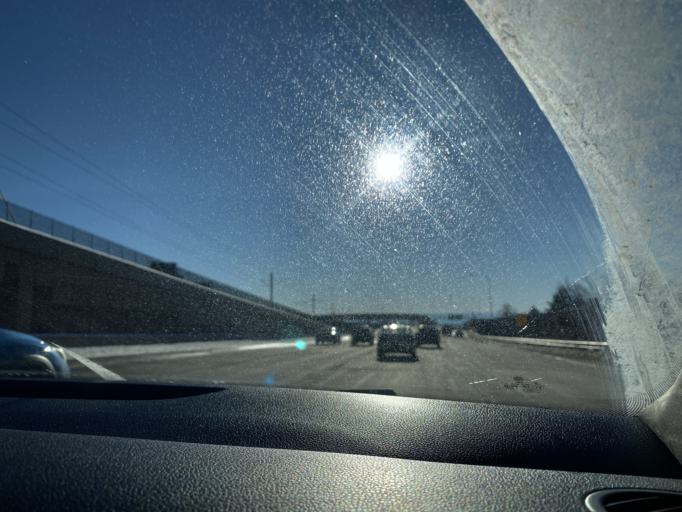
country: US
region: Colorado
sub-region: Adams County
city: Aurora
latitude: 39.6621
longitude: -104.8386
